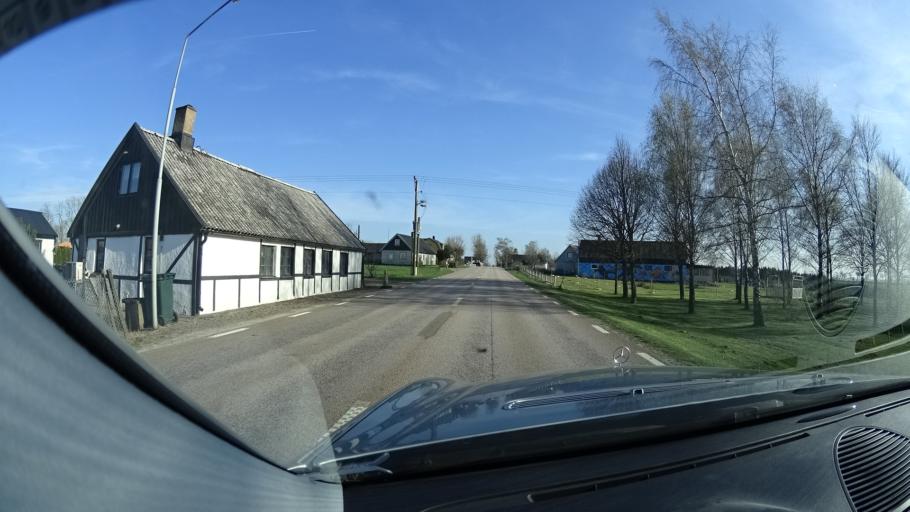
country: SE
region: Skane
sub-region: Landskrona
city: Asmundtorp
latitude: 55.9654
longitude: 12.9433
